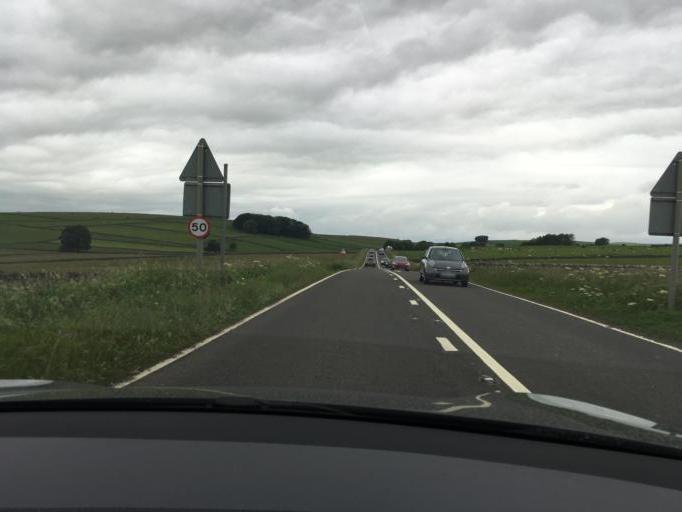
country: GB
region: England
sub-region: Derbyshire
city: Tideswell
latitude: 53.2964
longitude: -1.7930
